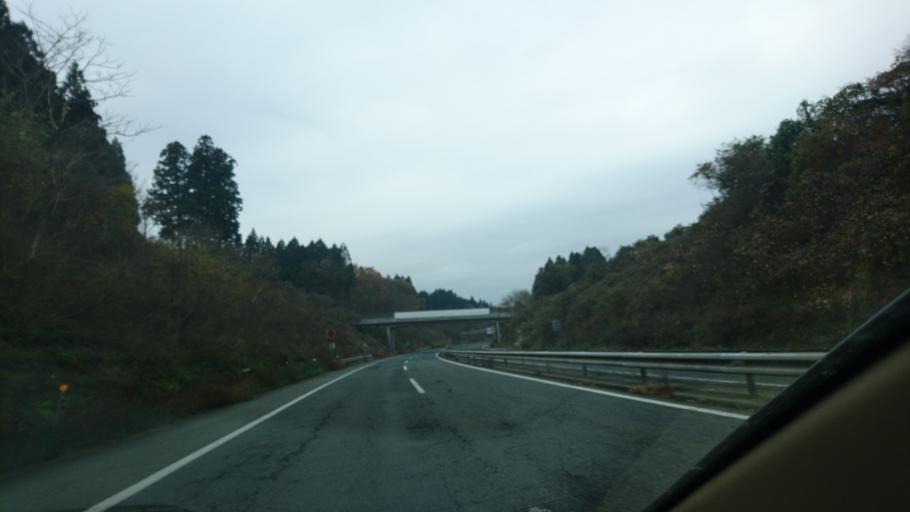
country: JP
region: Iwate
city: Kitakami
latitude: 39.2751
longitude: 141.0723
